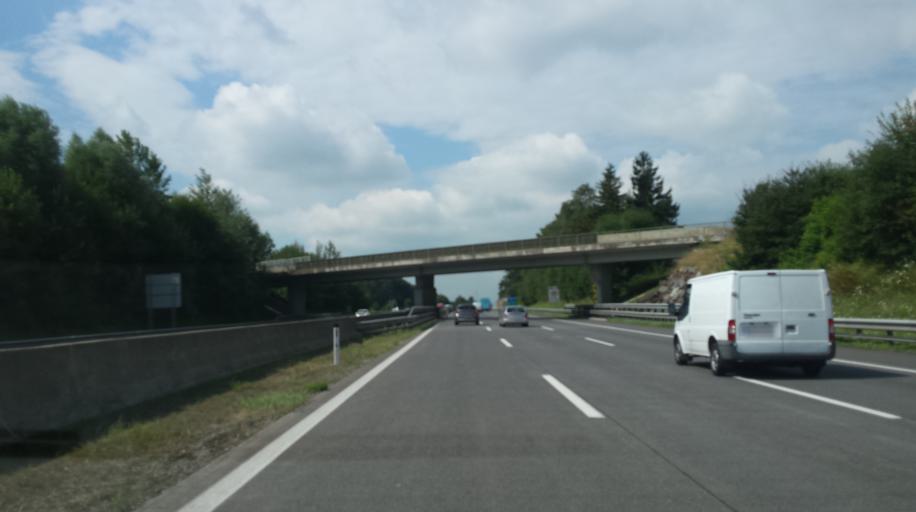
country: AT
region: Lower Austria
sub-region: Politischer Bezirk Amstetten
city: Amstetten
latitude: 48.1428
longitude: 14.8499
